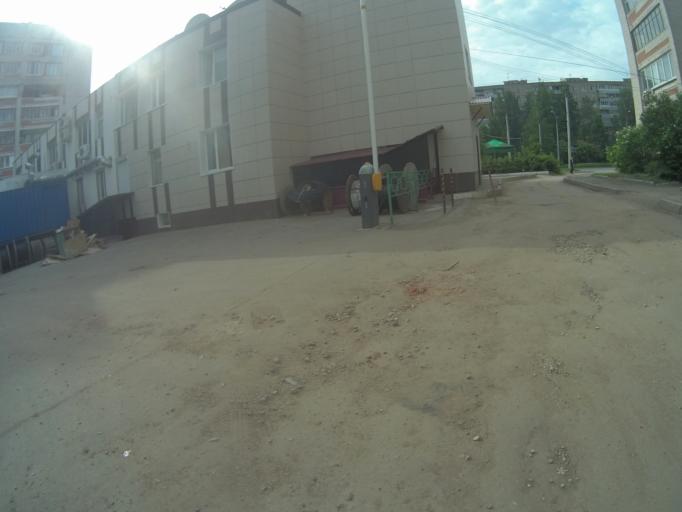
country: RU
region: Vladimir
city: Kommunar
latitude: 56.1659
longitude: 40.4600
